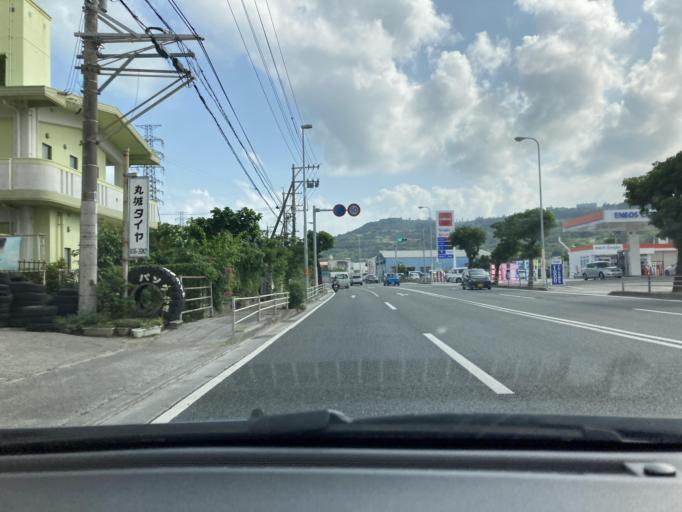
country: JP
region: Okinawa
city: Okinawa
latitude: 26.2999
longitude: 127.8089
